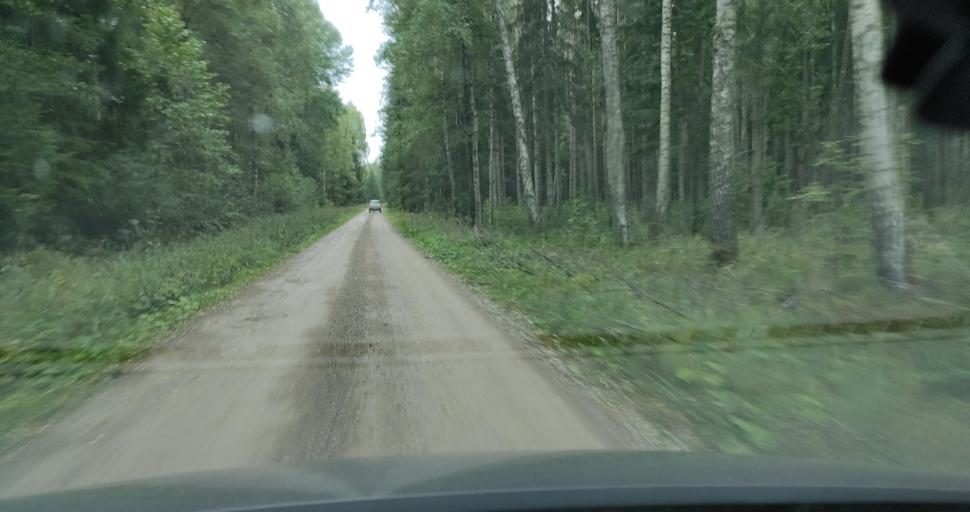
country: LV
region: Talsu Rajons
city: Stende
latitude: 57.0259
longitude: 22.3419
